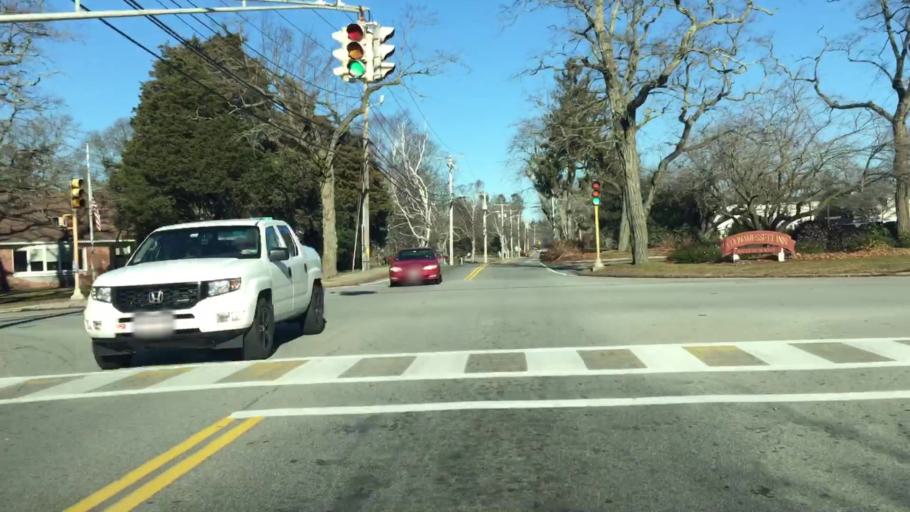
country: US
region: Massachusetts
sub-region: Barnstable County
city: Falmouth
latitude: 41.5605
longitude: -70.6105
